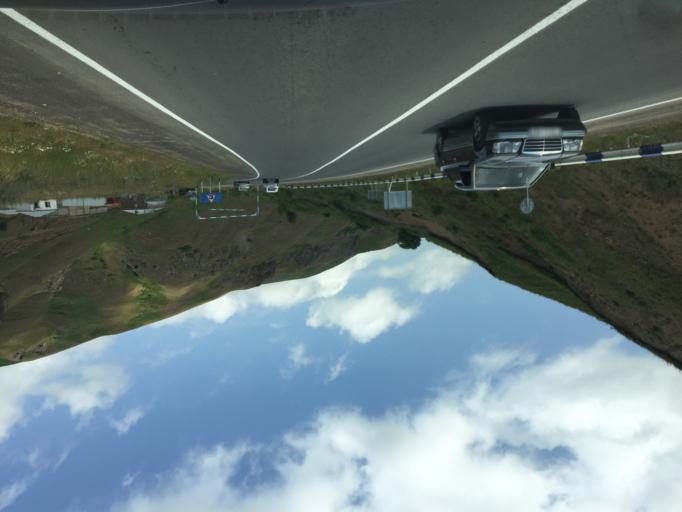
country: AM
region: Geghark'unik'i Marz
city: Tsovagyugh
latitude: 40.6524
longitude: 44.8941
